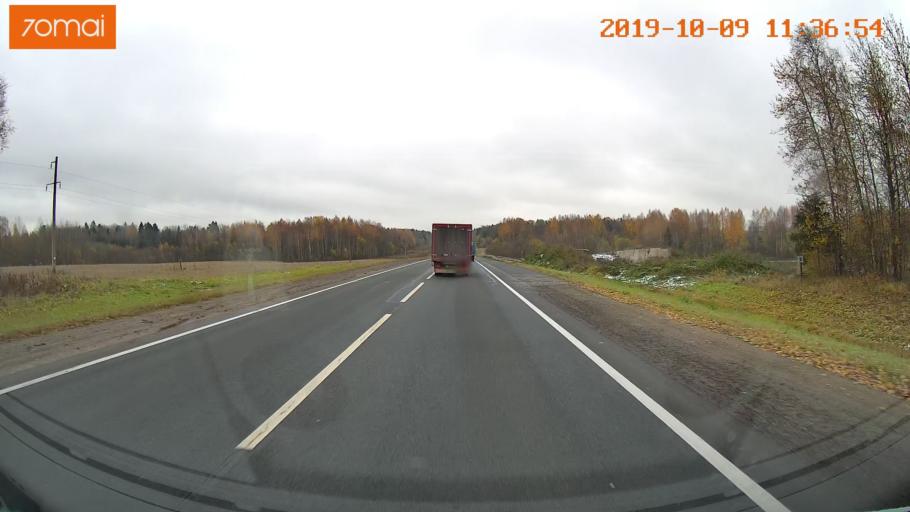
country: RU
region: Vologda
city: Gryazovets
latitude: 58.9850
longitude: 40.1418
